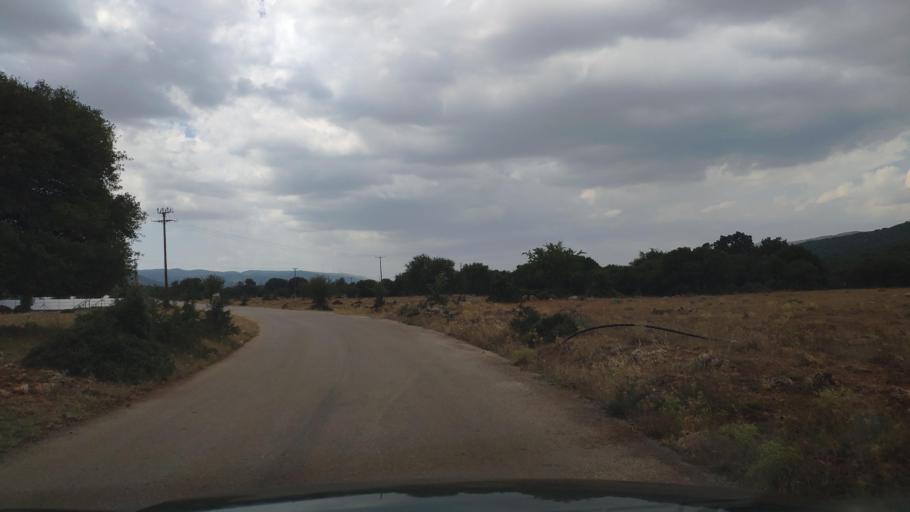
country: GR
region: Peloponnese
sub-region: Nomos Lakonias
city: Kariai
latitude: 37.3105
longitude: 22.4524
